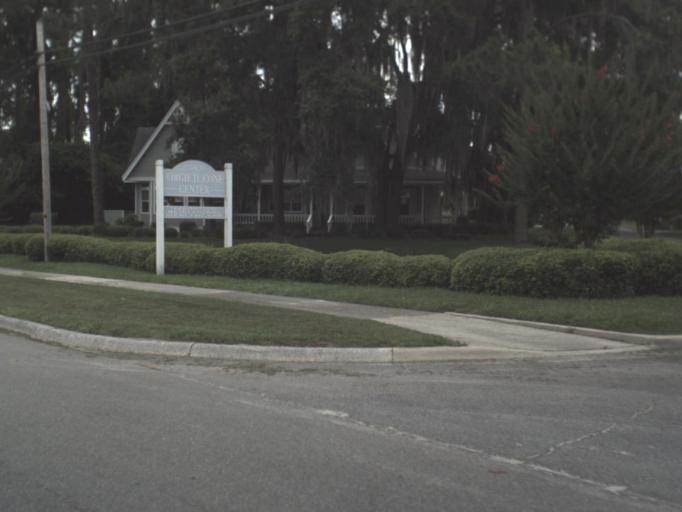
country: US
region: Florida
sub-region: Hamilton County
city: Jasper
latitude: 30.5211
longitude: -82.9557
